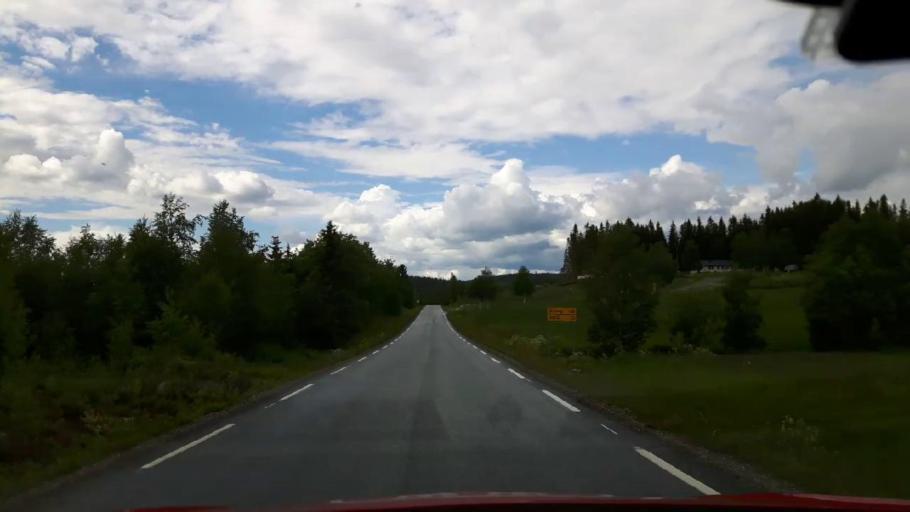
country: NO
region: Nord-Trondelag
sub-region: Lierne
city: Sandvika
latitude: 64.0952
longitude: 14.0405
